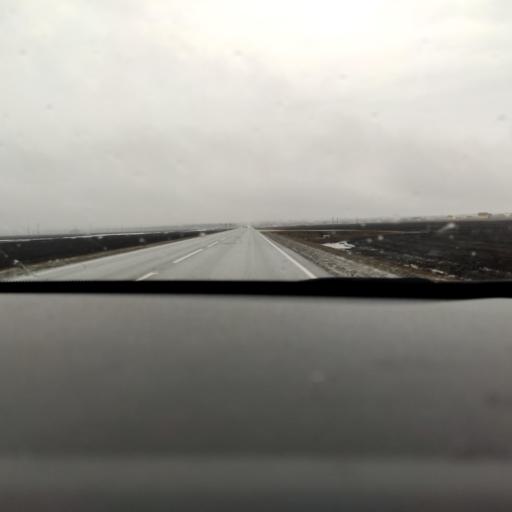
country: RU
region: Tatarstan
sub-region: Alekseyevskiy Rayon
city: Alekseyevskoye
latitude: 55.3095
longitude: 50.1773
